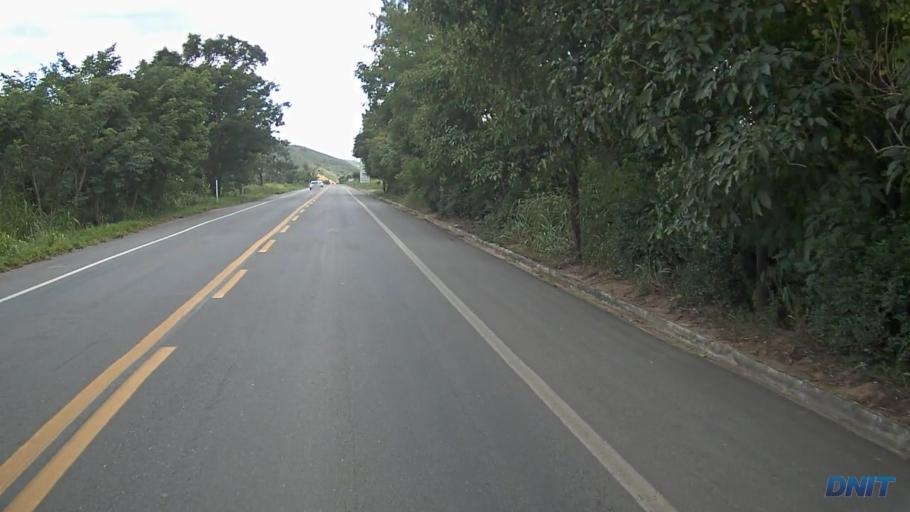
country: BR
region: Minas Gerais
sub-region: Governador Valadares
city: Governador Valadares
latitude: -18.9369
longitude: -42.0533
